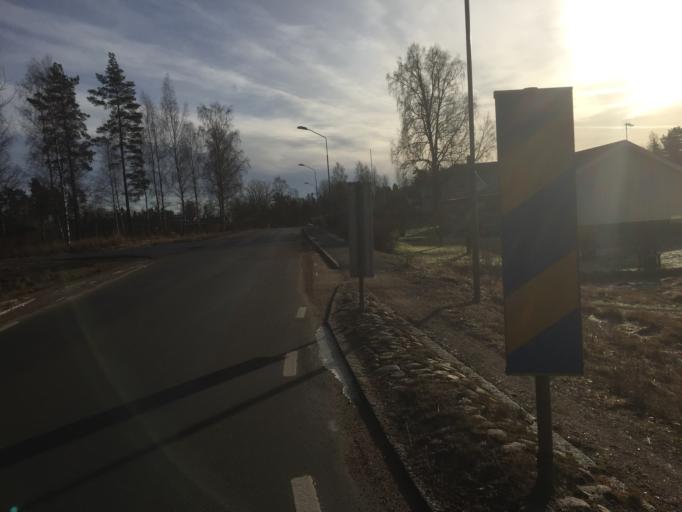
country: SE
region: Joenkoeping
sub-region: Aneby Kommun
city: Aneby
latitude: 57.8460
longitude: 14.7990
